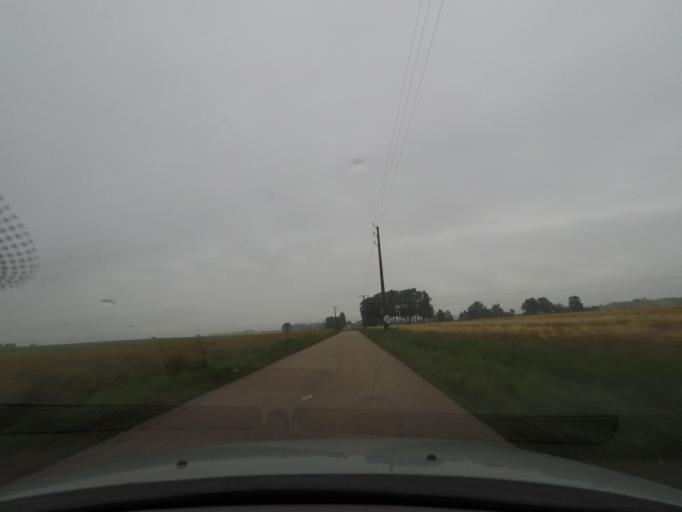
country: FR
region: Haute-Normandie
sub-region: Departement de la Seine-Maritime
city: Bosc-le-Hard
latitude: 49.5939
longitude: 1.2397
